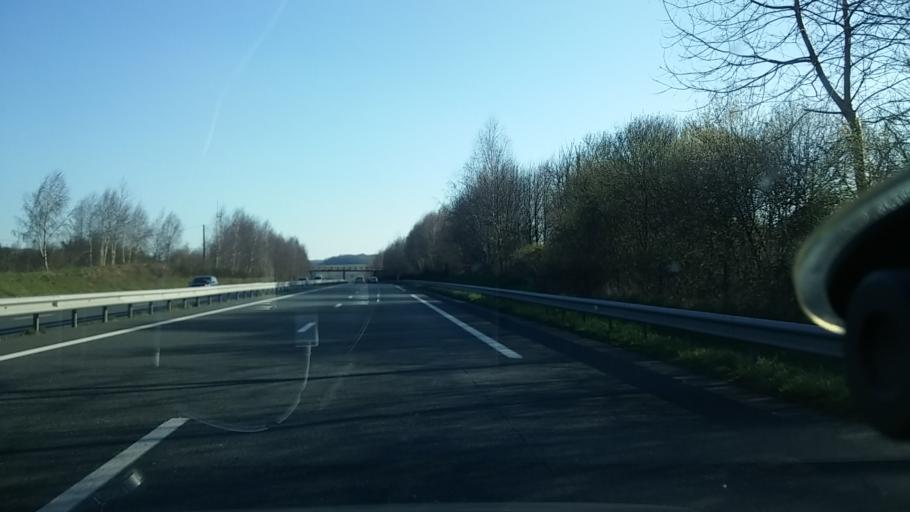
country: FR
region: Centre
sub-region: Departement de l'Indre
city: Chantome
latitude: 46.3895
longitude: 1.4498
